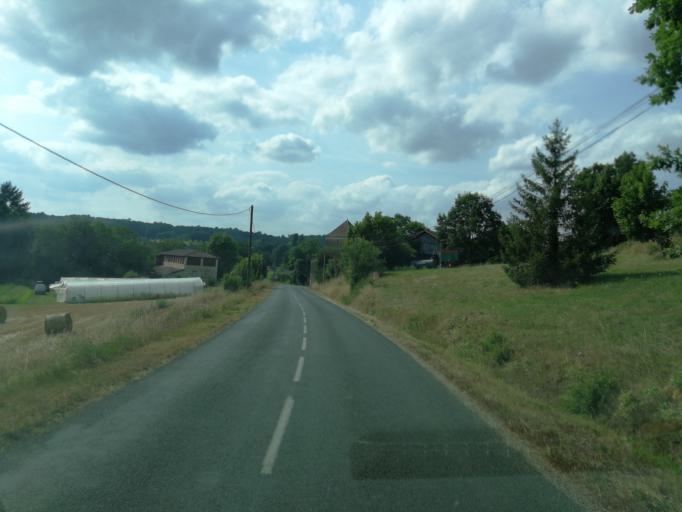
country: FR
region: Aquitaine
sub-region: Departement du Lot-et-Garonne
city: Fumel
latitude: 44.5258
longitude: 0.9453
